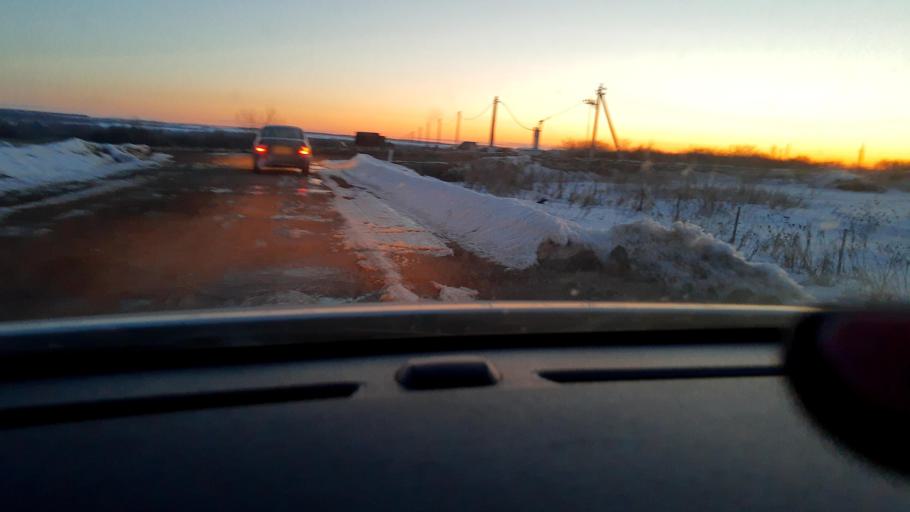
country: RU
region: Bashkortostan
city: Avdon
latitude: 54.3966
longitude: 55.7016
